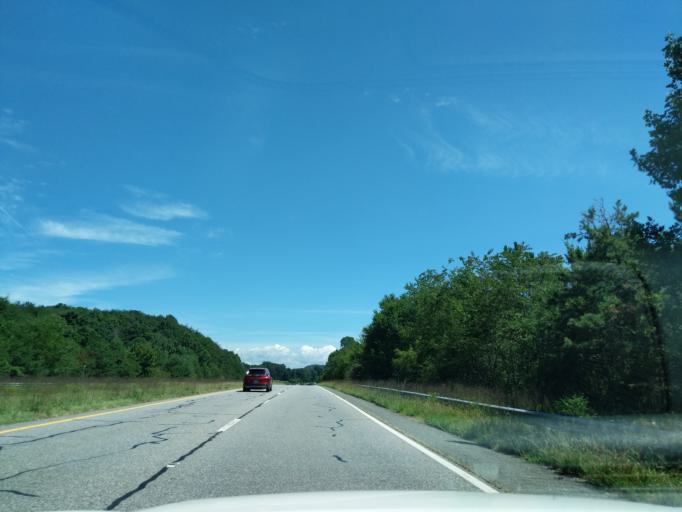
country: US
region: Georgia
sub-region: Fannin County
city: Blue Ridge
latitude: 34.8899
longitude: -84.2307
